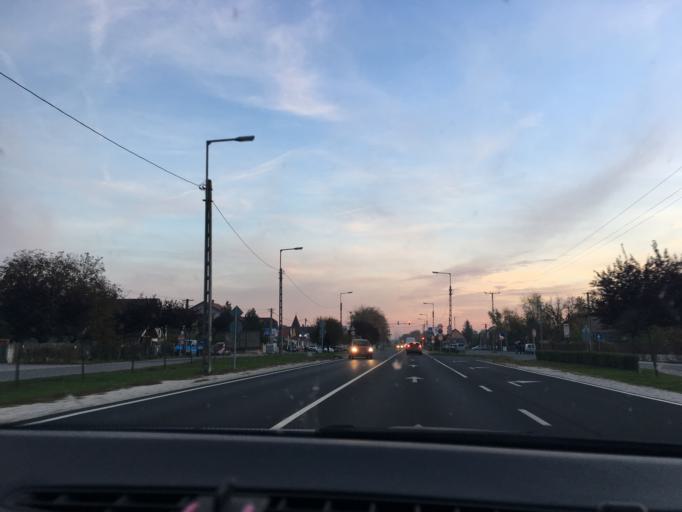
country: HU
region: Hajdu-Bihar
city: Hajduhadhaz
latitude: 47.6450
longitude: 21.6599
